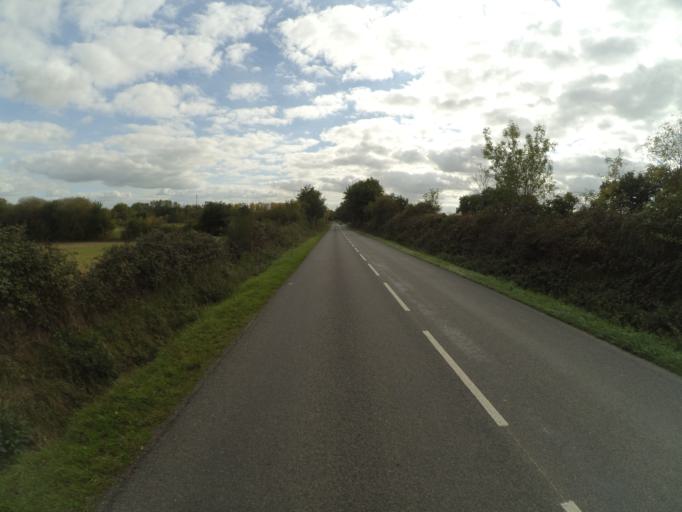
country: FR
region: Pays de la Loire
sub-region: Departement de la Loire-Atlantique
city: Bouvron
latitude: 47.4662
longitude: -1.8357
